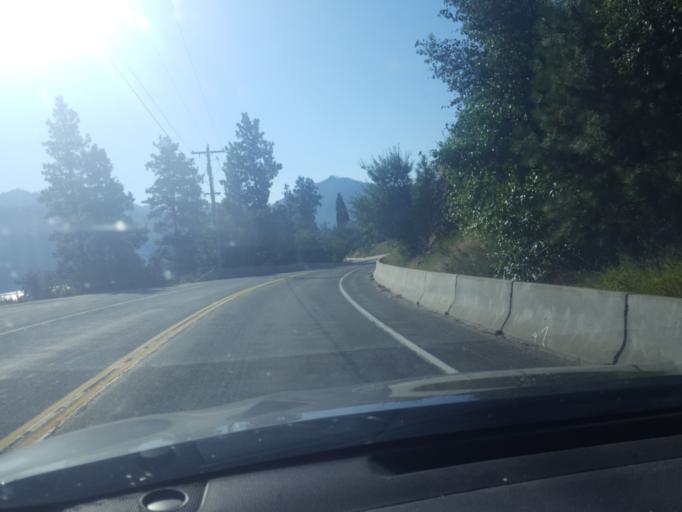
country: US
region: Washington
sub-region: Chelan County
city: Granite Falls
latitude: 47.9924
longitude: -120.2513
